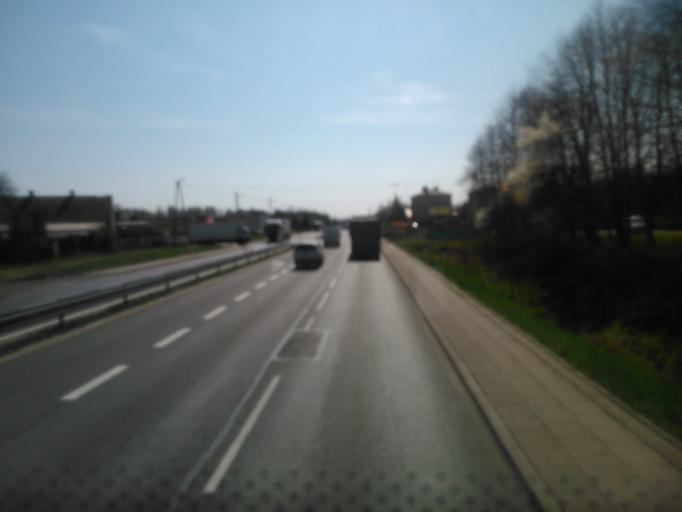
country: PL
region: Silesian Voivodeship
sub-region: Powiat czestochowski
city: Kamienica Polska
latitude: 50.6931
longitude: 19.1365
